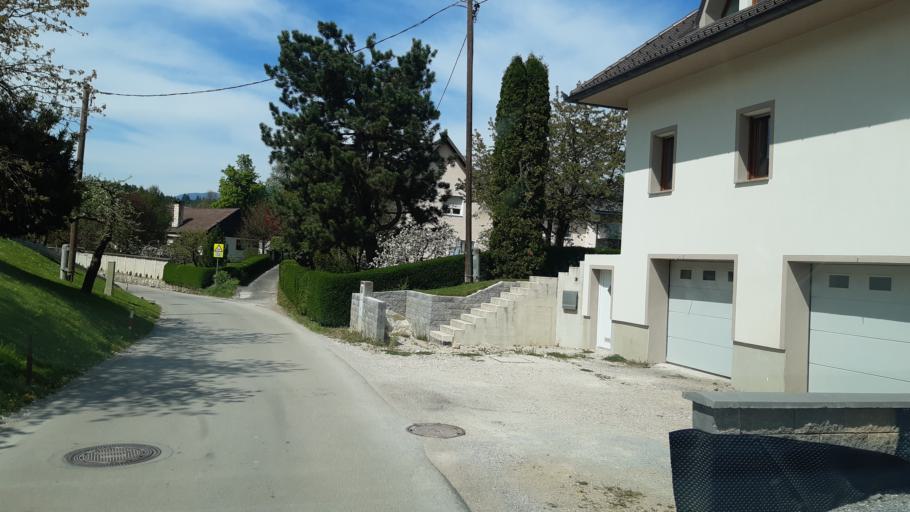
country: SI
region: Domzale
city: Radomlje
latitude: 46.1792
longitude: 14.6331
